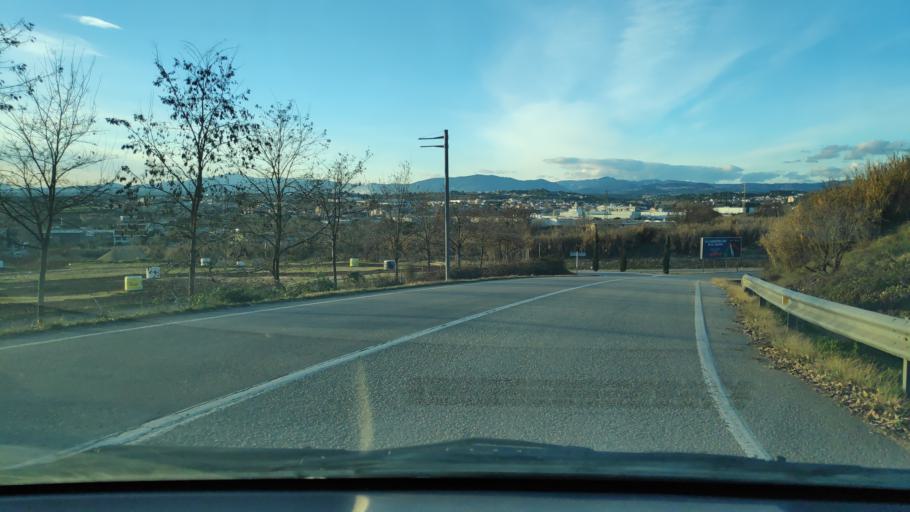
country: ES
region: Catalonia
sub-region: Provincia de Barcelona
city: Montmelo
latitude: 41.5674
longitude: 2.2518
